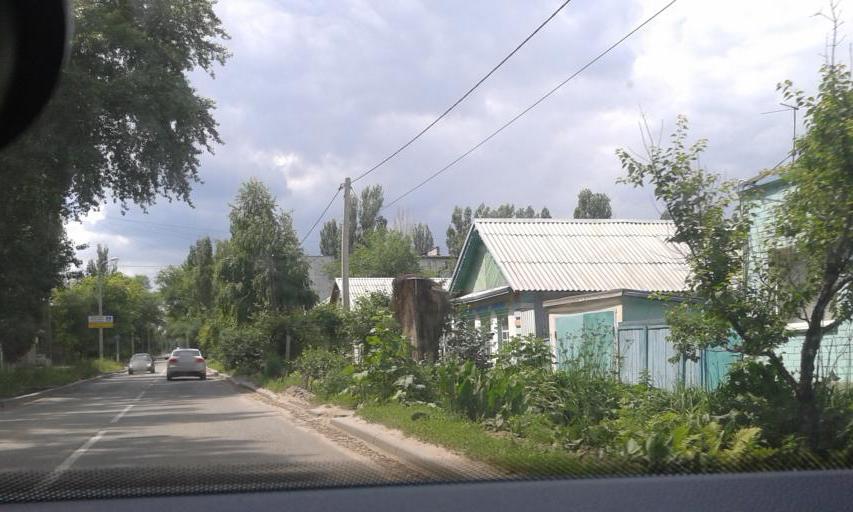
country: RU
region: Volgograd
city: Gorodishche
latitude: 48.7725
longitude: 44.4901
